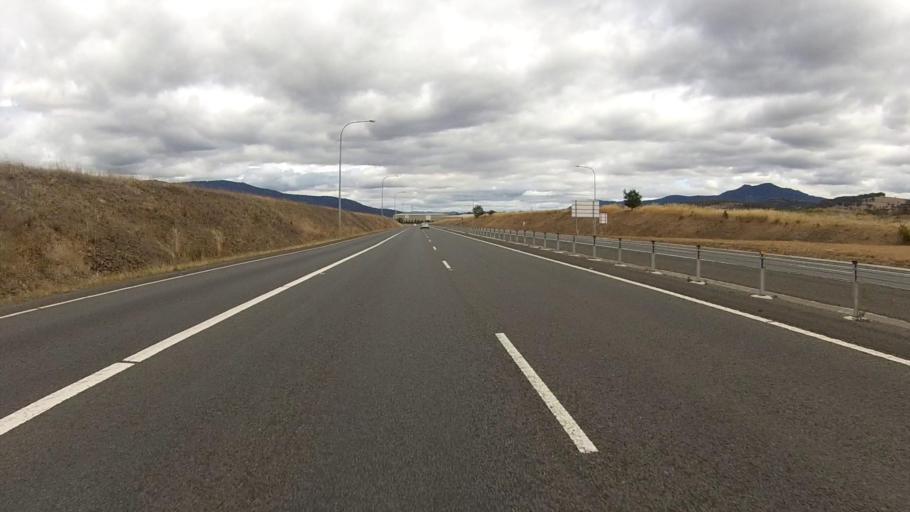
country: AU
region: Tasmania
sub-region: Brighton
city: Bridgewater
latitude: -42.7147
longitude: 147.2438
